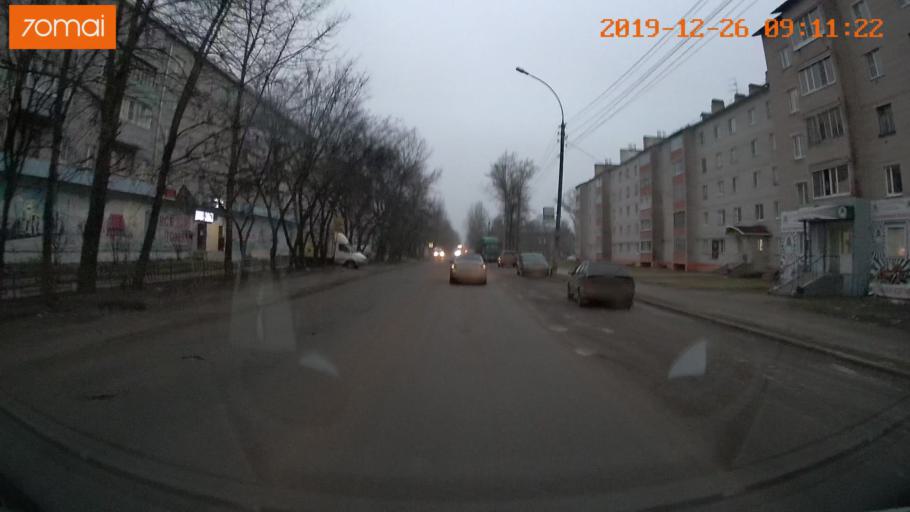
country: RU
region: Vologda
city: Gryazovets
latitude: 58.8757
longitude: 40.2526
